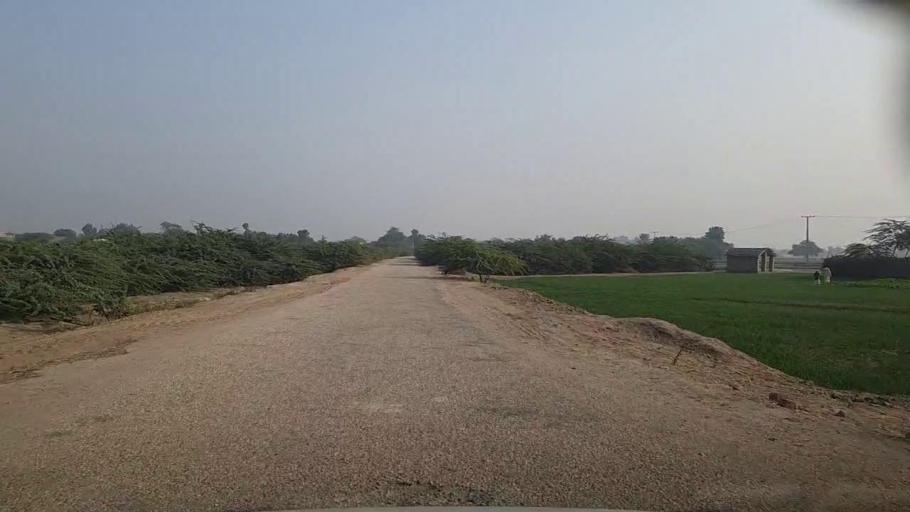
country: PK
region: Sindh
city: Kandiari
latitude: 27.0439
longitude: 68.4744
